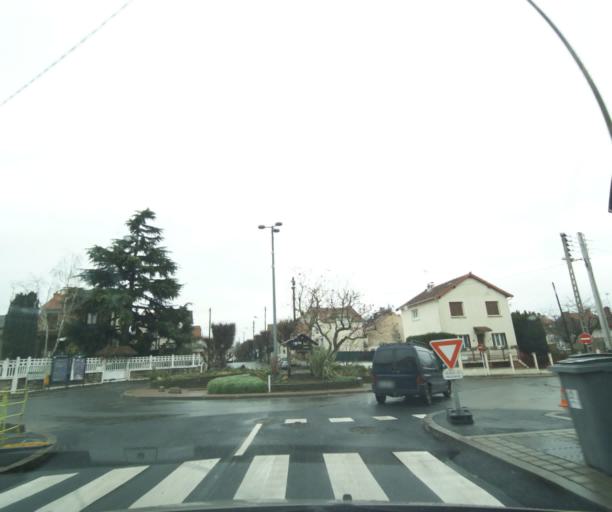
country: FR
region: Ile-de-France
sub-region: Departement du Val-de-Marne
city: Ablon-sur-Seine
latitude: 48.7392
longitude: 2.4175
